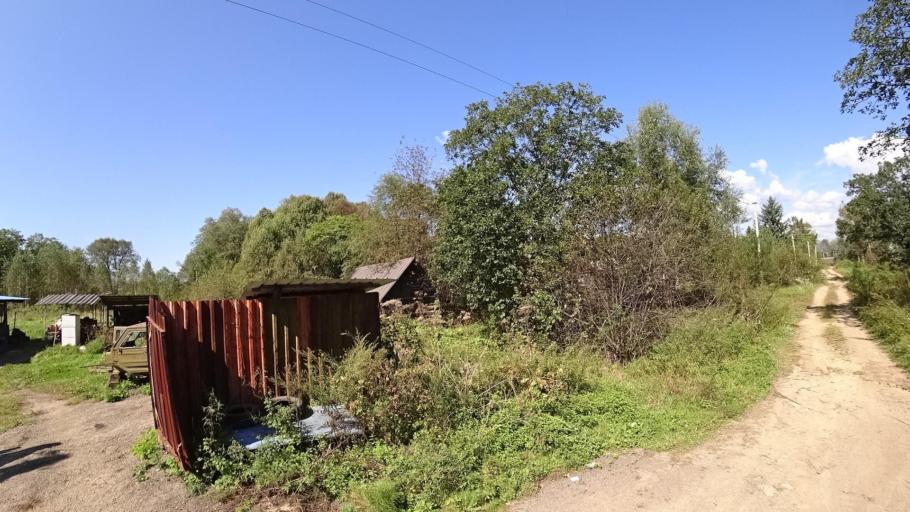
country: RU
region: Jewish Autonomous Oblast
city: Londoko
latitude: 49.0122
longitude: 132.2299
